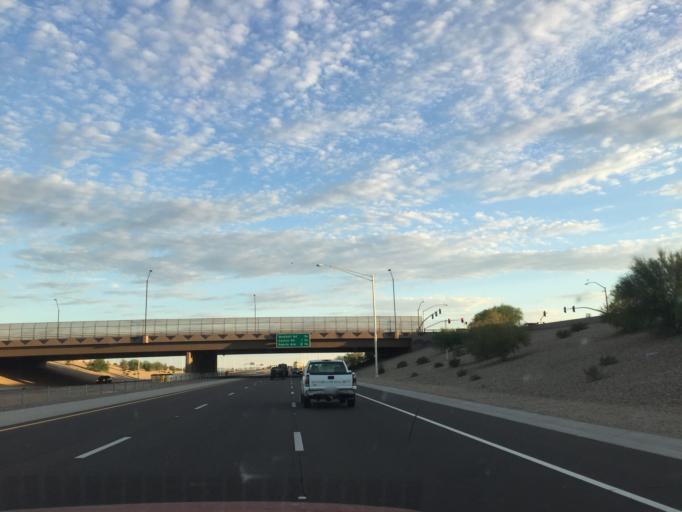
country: US
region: Arizona
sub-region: Maricopa County
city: Citrus Park
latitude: 33.6256
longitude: -112.4182
